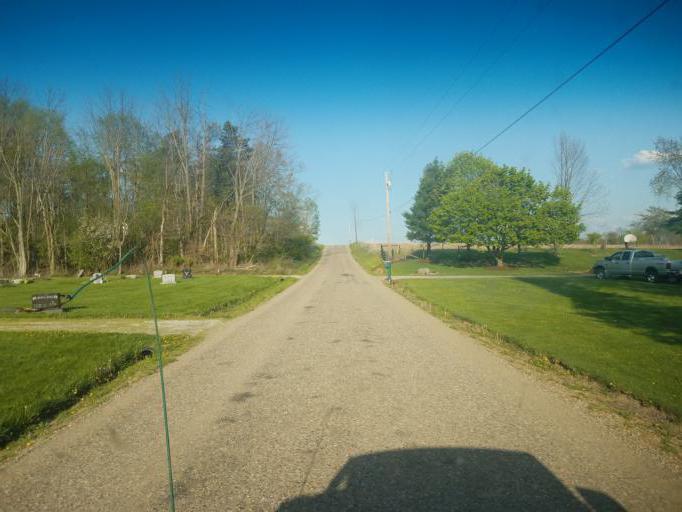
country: US
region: Ohio
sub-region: Wayne County
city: Shreve
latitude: 40.6056
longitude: -82.0239
